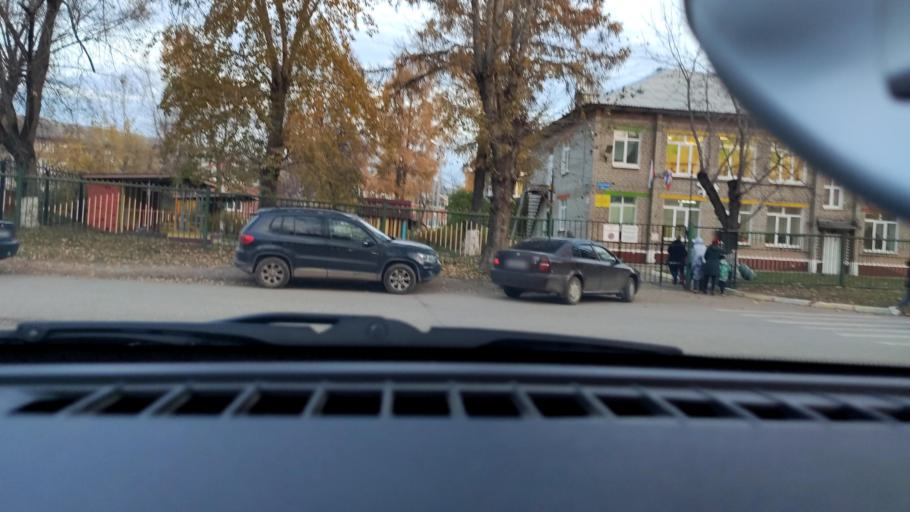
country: RU
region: Perm
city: Perm
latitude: 57.9859
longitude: 56.2038
